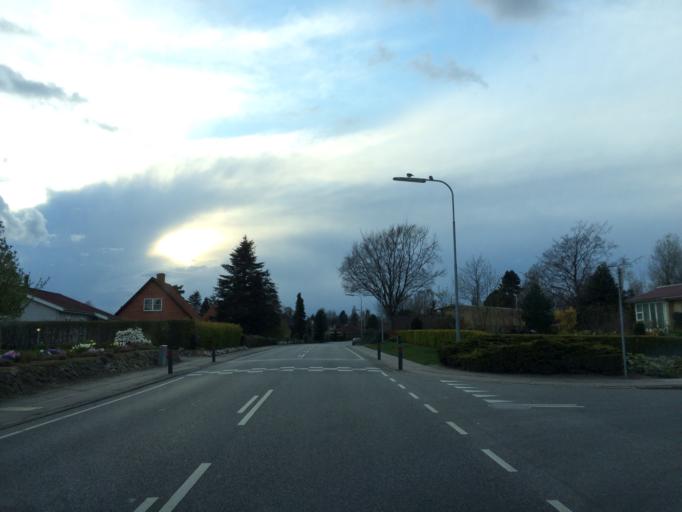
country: DK
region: South Denmark
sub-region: Odense Kommune
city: Bellinge
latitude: 55.3334
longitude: 10.3206
